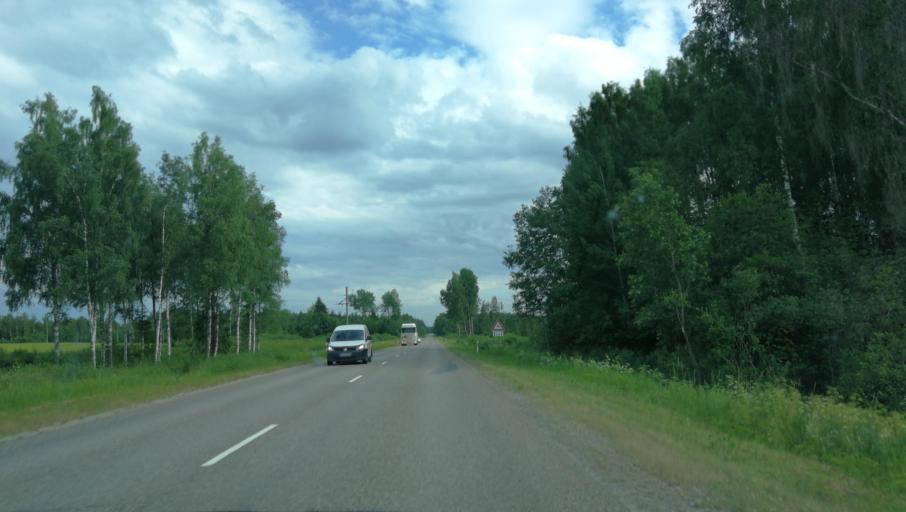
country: LV
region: Naukseni
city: Naukseni
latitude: 57.8234
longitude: 25.3960
